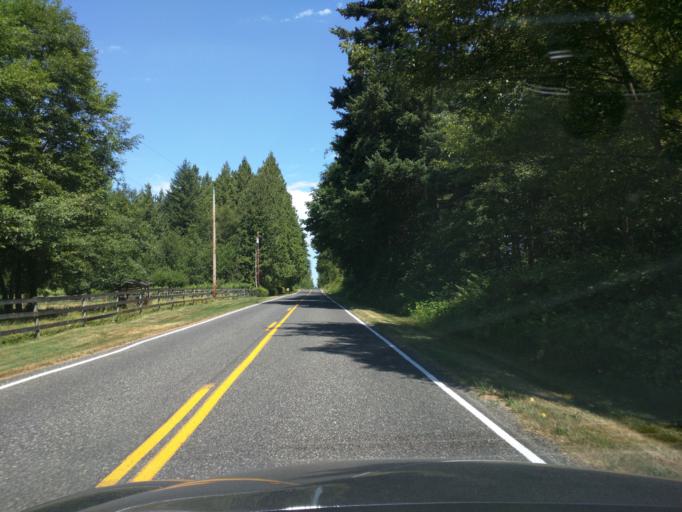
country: CA
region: British Columbia
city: Langley
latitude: 48.9709
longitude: -122.5963
